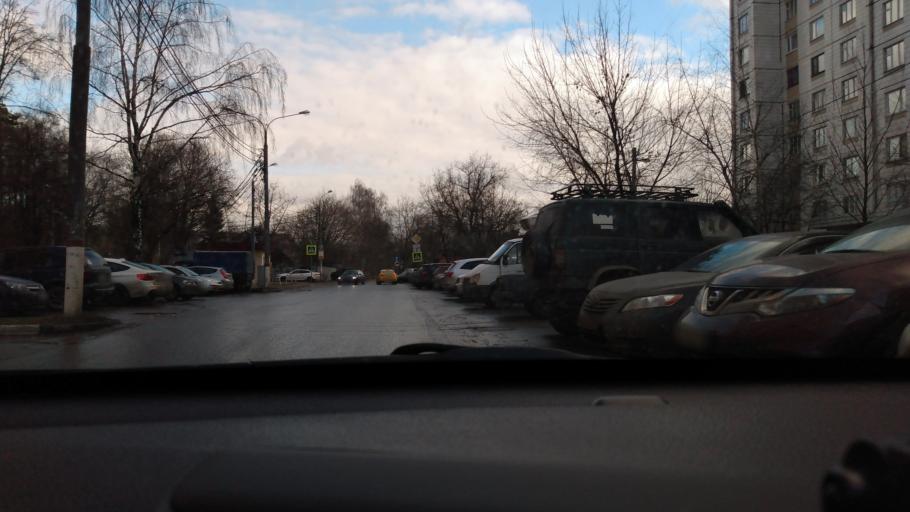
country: RU
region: Moskovskaya
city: Yubileyny
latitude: 55.9217
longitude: 37.8716
